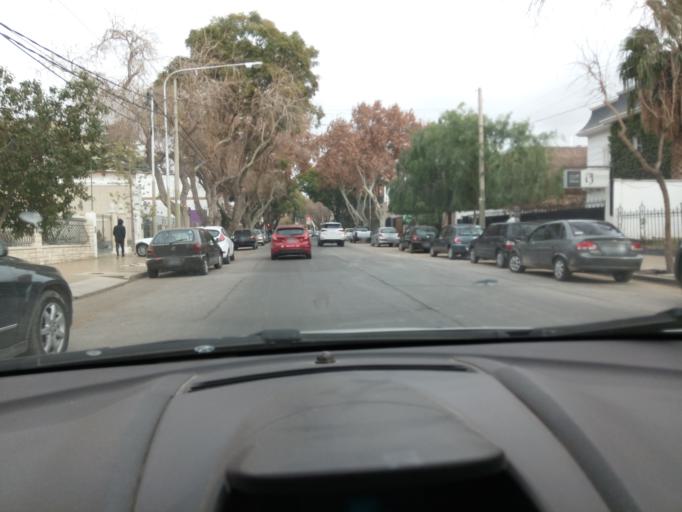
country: AR
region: San Juan
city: San Juan
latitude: -31.5339
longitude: -68.5340
